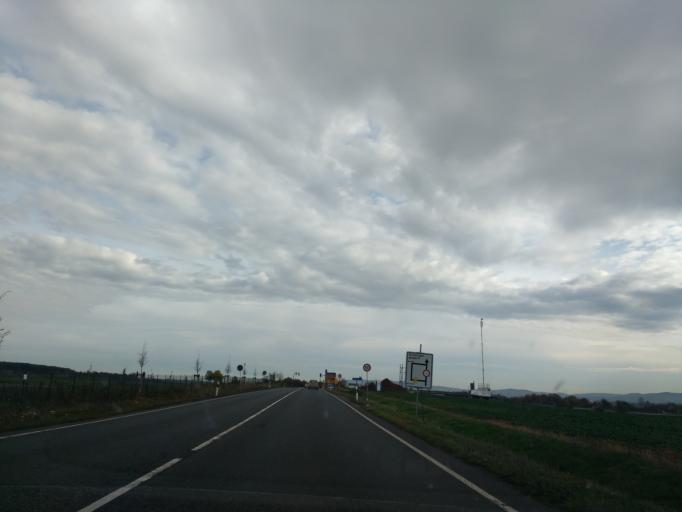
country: DE
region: Thuringia
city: Urbach
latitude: 51.4784
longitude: 10.8709
